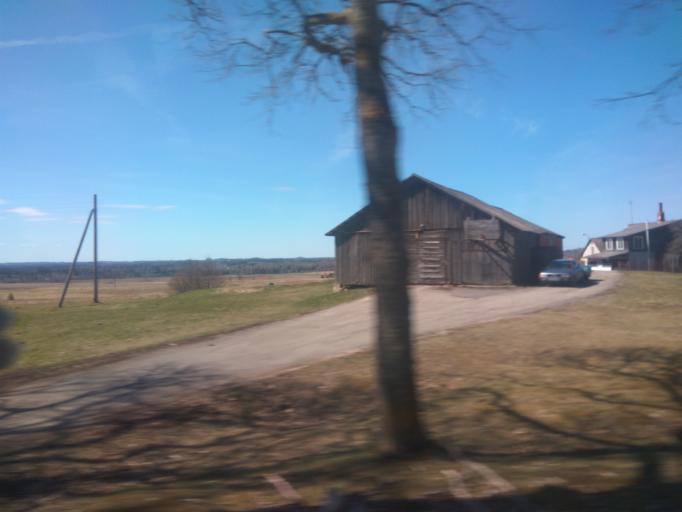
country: LV
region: Aluksnes Rajons
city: Aluksne
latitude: 57.5402
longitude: 27.0534
